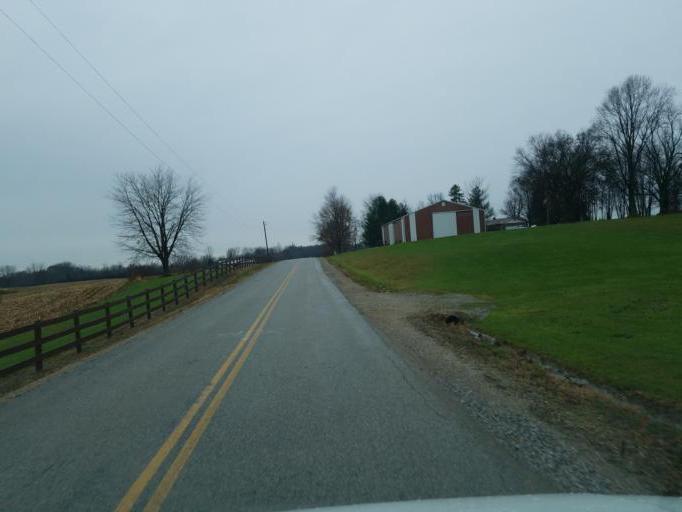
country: US
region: Ohio
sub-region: Knox County
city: Centerburg
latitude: 40.3228
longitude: -82.7718
